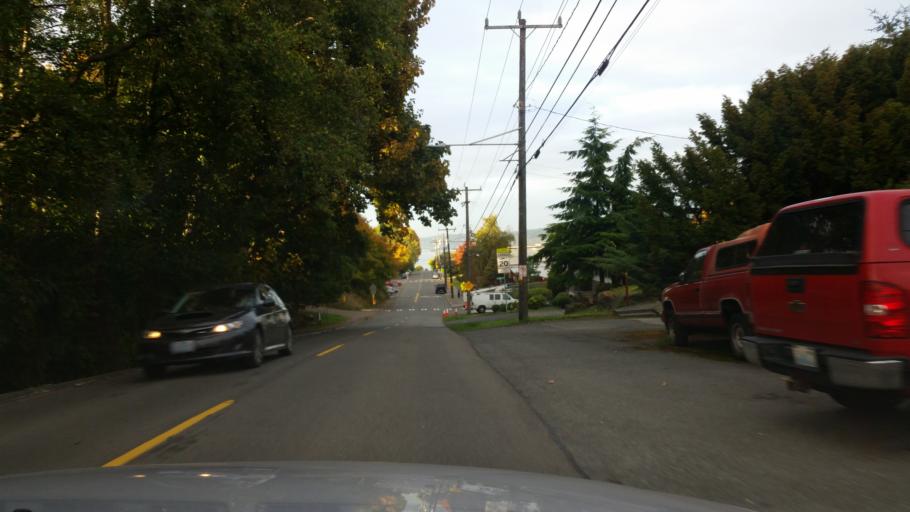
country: US
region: Washington
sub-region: King County
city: Shoreline
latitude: 47.6934
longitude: -122.3876
